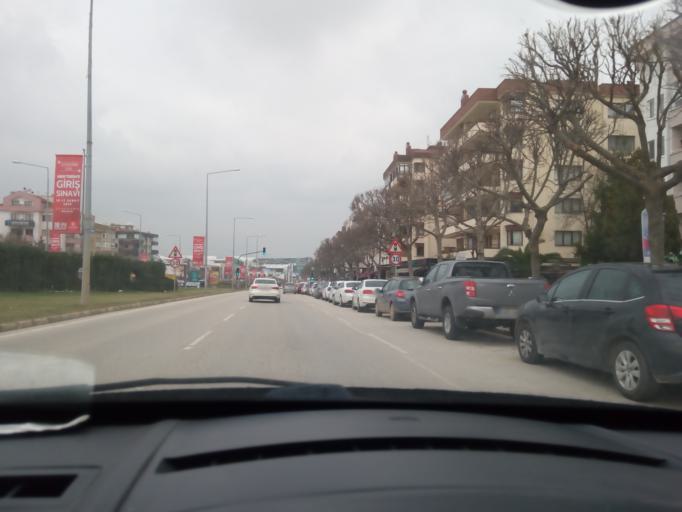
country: TR
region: Bursa
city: Yildirim
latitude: 40.2257
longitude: 28.9796
